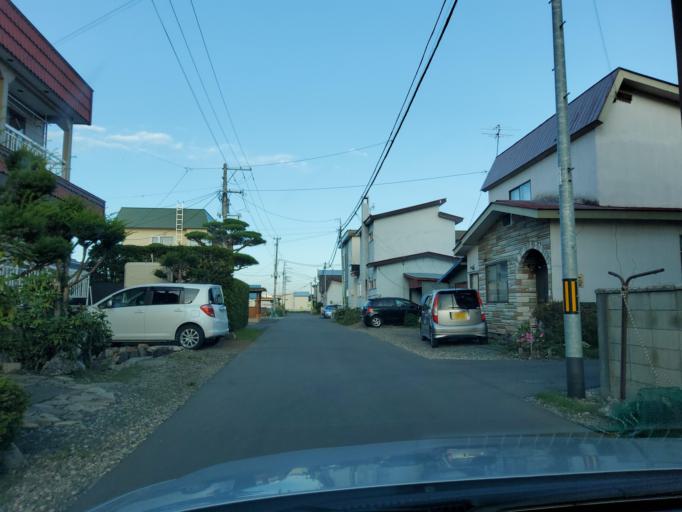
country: JP
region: Hokkaido
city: Obihiro
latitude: 42.9158
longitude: 143.1794
